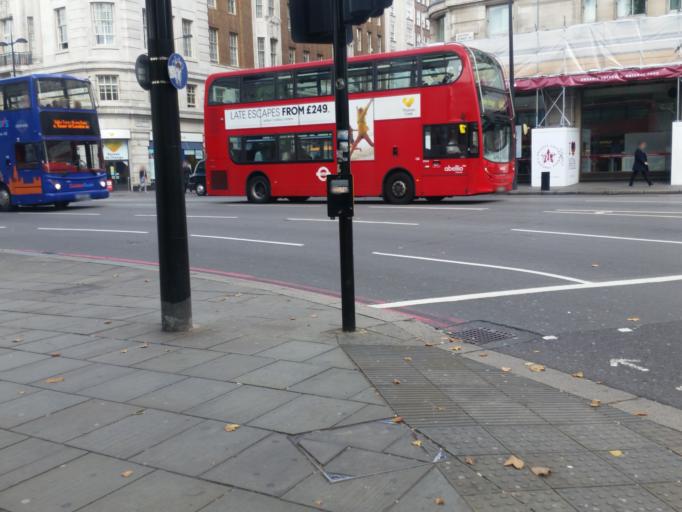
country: GB
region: England
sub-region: Greater London
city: Bayswater
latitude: 51.5133
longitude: -0.1588
